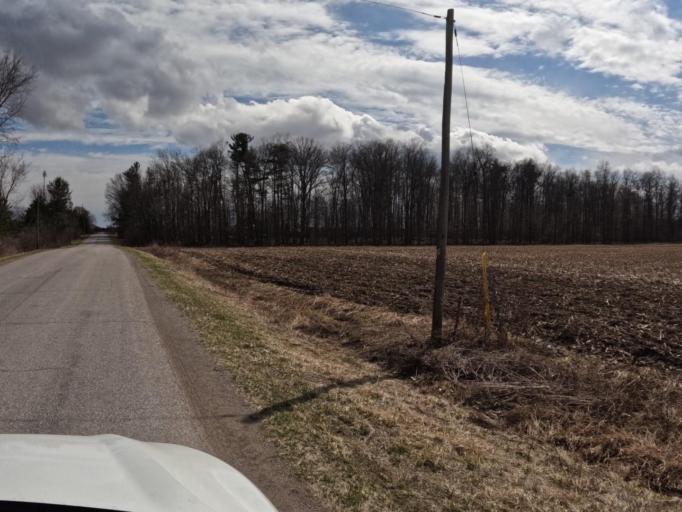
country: CA
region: Ontario
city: Norfolk County
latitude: 42.8747
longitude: -80.1955
